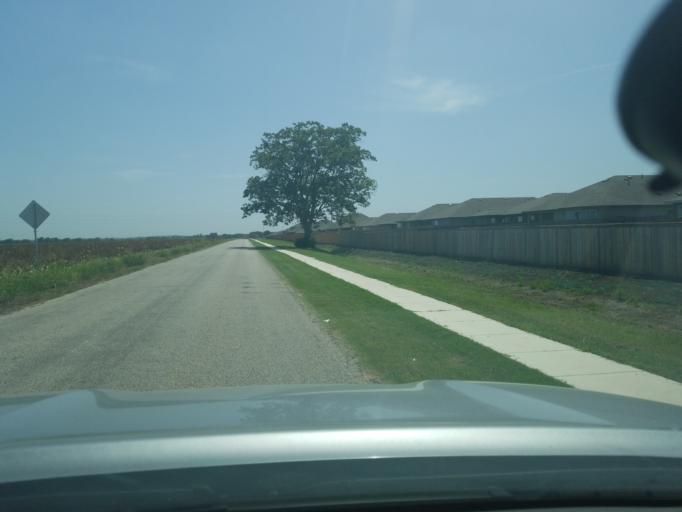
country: US
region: Texas
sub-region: Guadalupe County
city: Lake Dunlap
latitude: 29.6723
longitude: -98.0326
